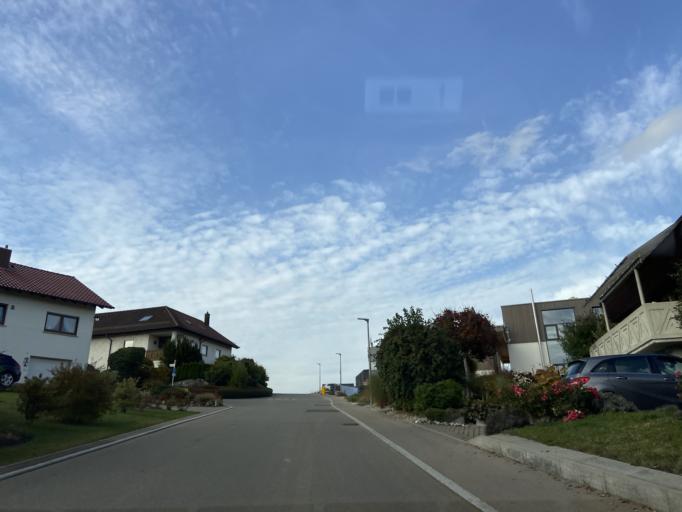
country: DE
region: Baden-Wuerttemberg
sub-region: Tuebingen Region
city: Bingen
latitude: 48.1027
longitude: 9.2852
